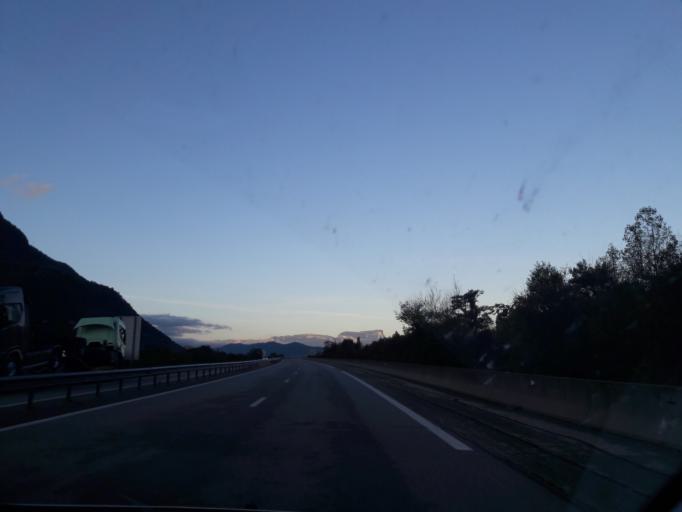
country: FR
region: Rhone-Alpes
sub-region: Departement de la Savoie
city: Aiton
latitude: 45.5580
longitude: 6.2604
